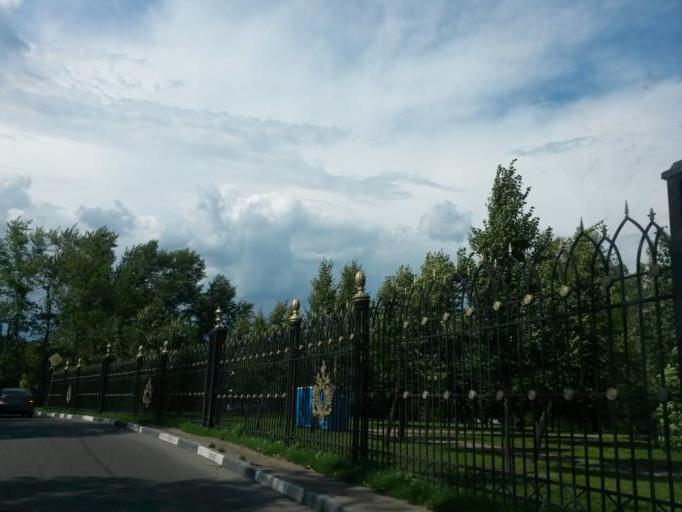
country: RU
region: Moscow
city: Orekhovo-Borisovo Severnoye
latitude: 55.6110
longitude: 37.6703
